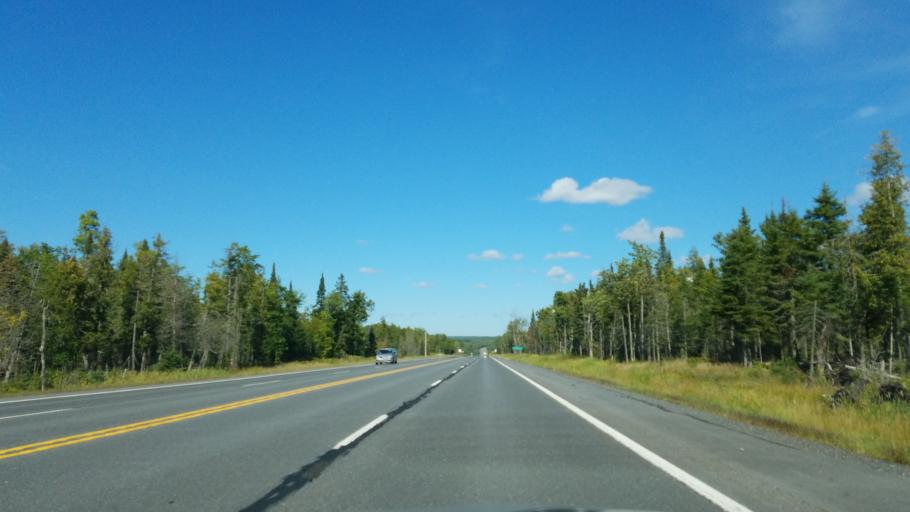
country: US
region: Michigan
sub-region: Baraga County
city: L'Anse
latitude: 46.5617
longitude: -88.5084
